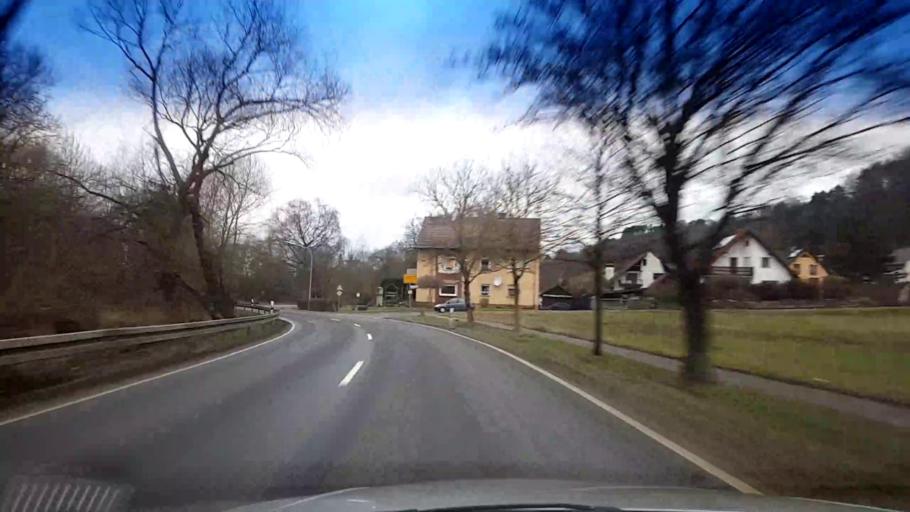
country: DE
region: Bavaria
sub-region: Upper Franconia
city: Wattendorf
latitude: 50.0678
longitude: 11.0665
